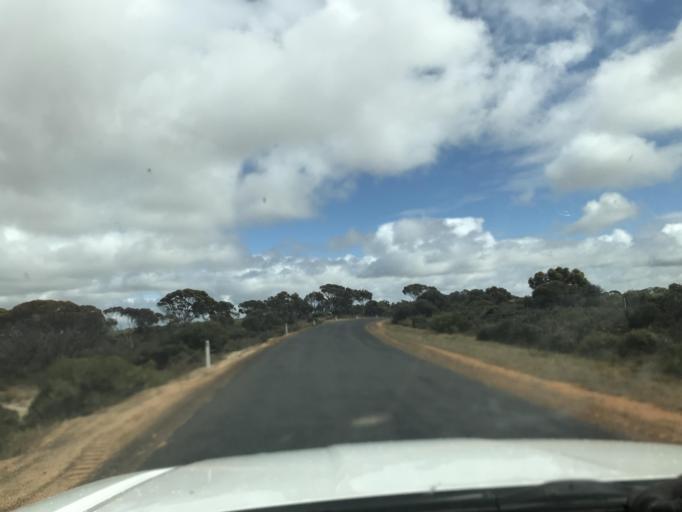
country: AU
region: South Australia
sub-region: Tatiara
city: Bordertown
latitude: -36.1761
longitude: 141.1529
